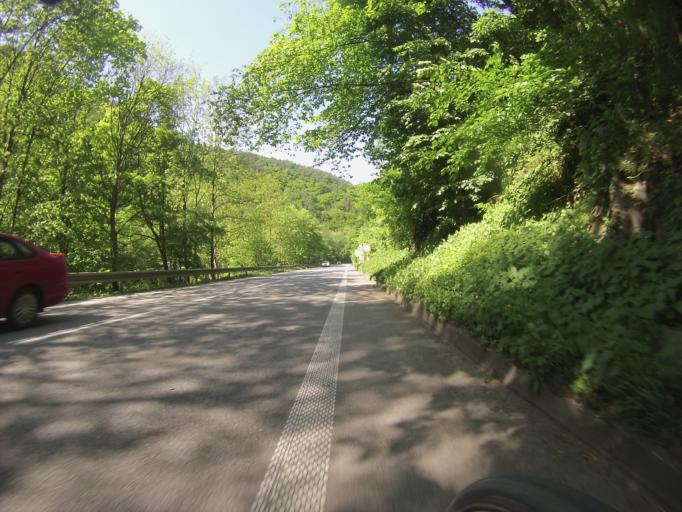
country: CZ
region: South Moravian
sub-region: Okres Blansko
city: Blansko
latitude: 49.3332
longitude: 16.6450
